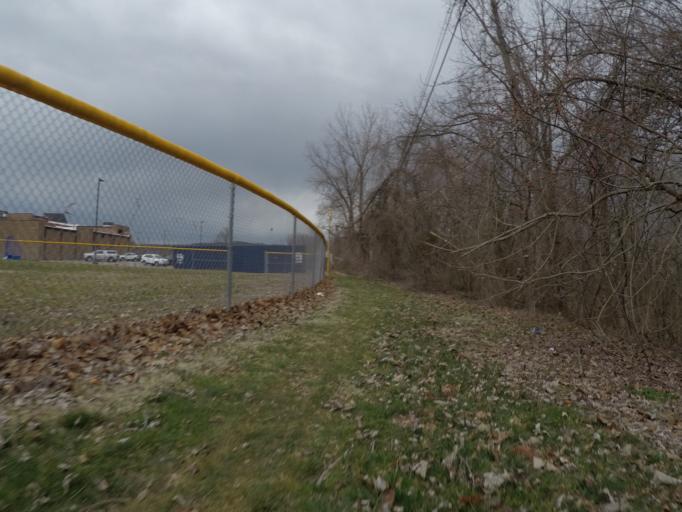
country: US
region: West Virginia
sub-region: Cabell County
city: Huntington
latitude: 38.4233
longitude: -82.4874
